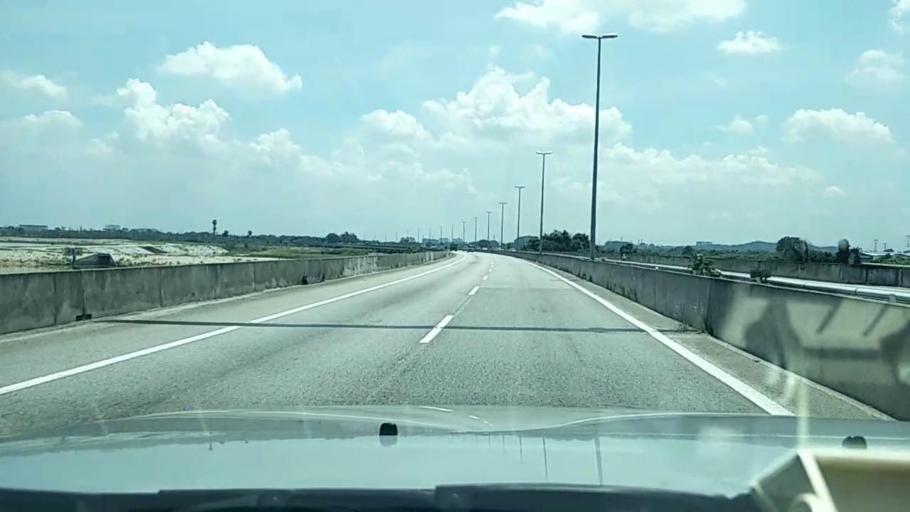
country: MY
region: Putrajaya
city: Putrajaya
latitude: 2.9456
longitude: 101.6481
